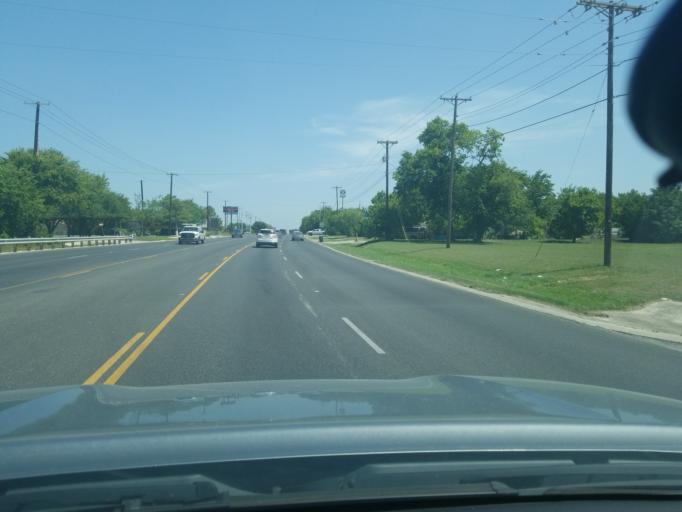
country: US
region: Texas
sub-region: Guadalupe County
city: Lake Dunlap
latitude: 29.6866
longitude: -98.0673
